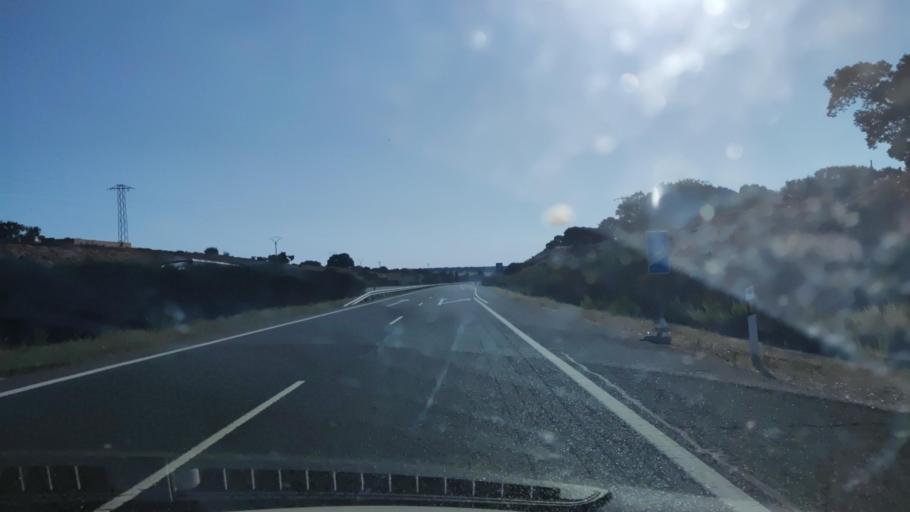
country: ES
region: Castille and Leon
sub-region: Provincia de Salamanca
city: San Munoz
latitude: 40.8115
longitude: -6.1416
